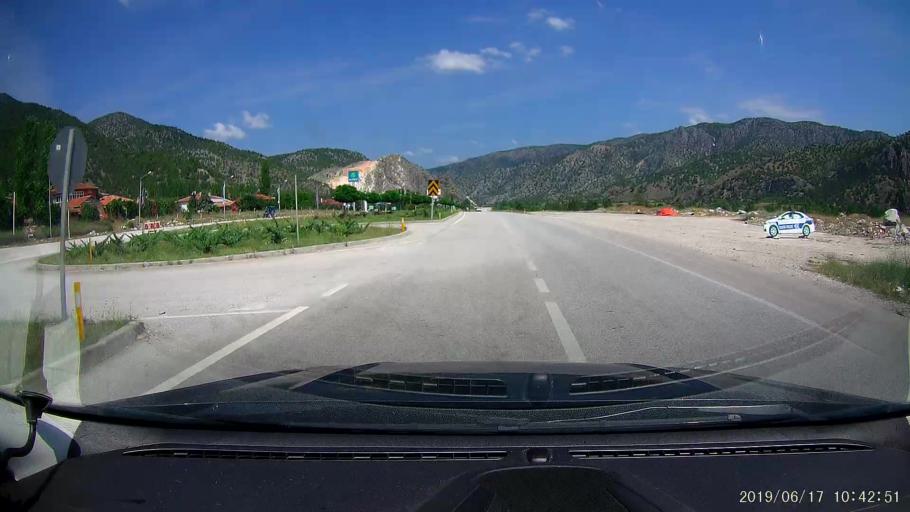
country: TR
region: Corum
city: Hacihamza
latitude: 41.0537
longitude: 34.5458
